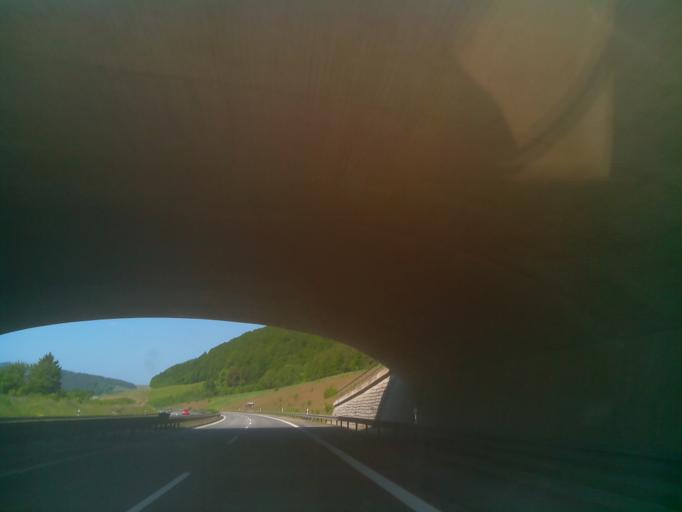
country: DE
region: Thuringia
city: Ellingshausen
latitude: 50.5410
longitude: 10.4775
